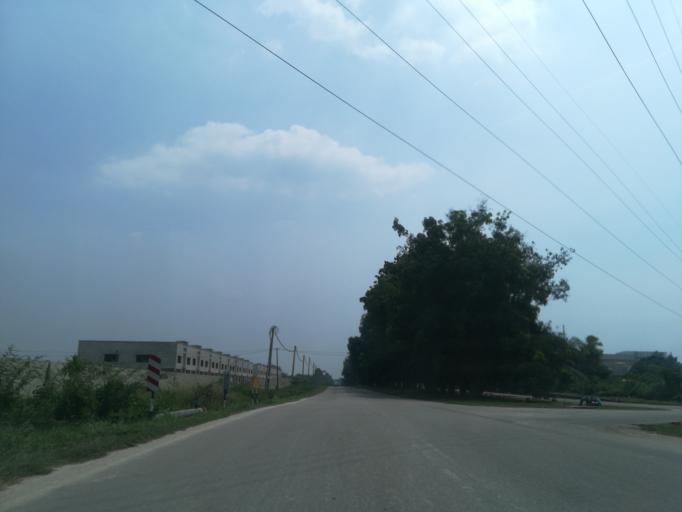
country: MY
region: Penang
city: Tasek Glugor
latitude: 5.4517
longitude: 100.5399
